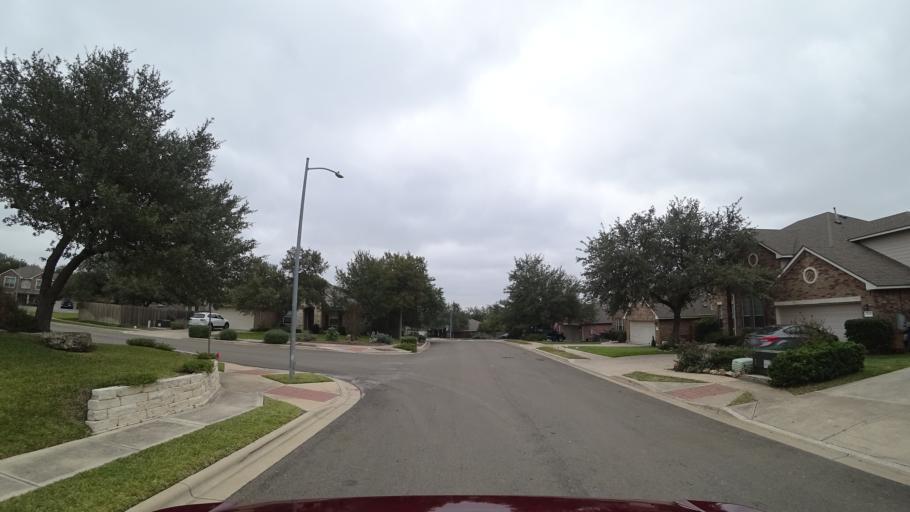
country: US
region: Texas
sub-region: Williamson County
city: Anderson Mill
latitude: 30.4377
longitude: -97.8312
